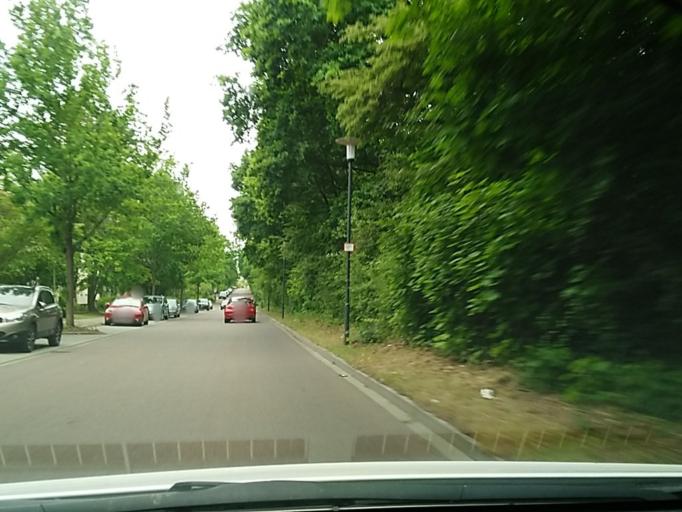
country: DE
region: Saxony-Anhalt
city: Halle Neustadt
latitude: 51.5002
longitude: 11.9298
